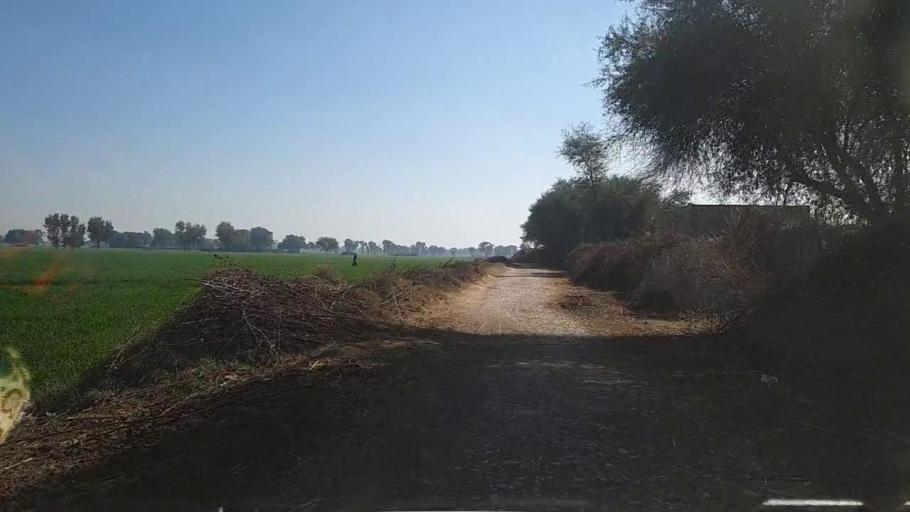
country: PK
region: Sindh
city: Khairpur
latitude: 28.0482
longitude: 69.8179
